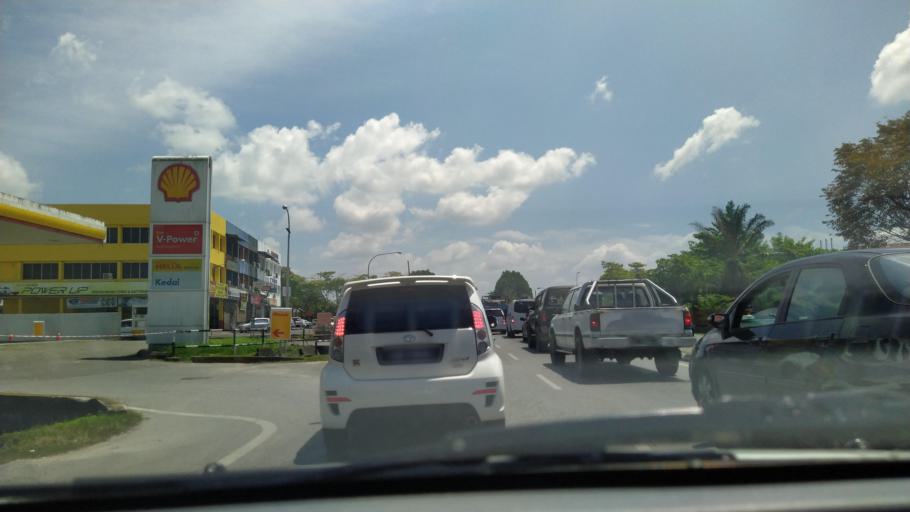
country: MY
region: Sarawak
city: Sibu
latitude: 2.2960
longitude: 111.8414
